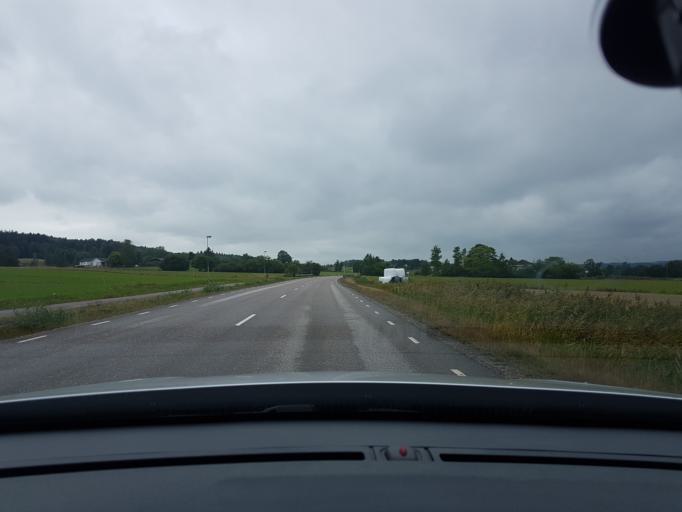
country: SE
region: Vaestra Goetaland
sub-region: Ale Kommun
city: Skepplanda
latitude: 57.9742
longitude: 12.1817
